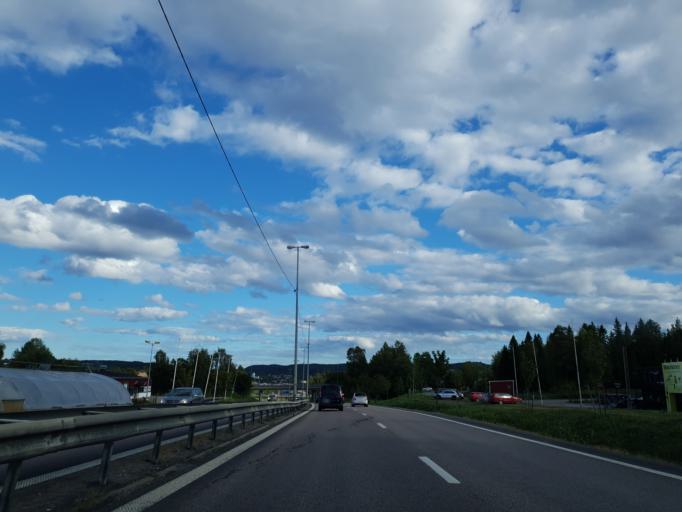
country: SE
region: Vaesternorrland
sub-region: Haernoesands Kommun
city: Haernoesand
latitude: 62.6413
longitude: 17.9137
